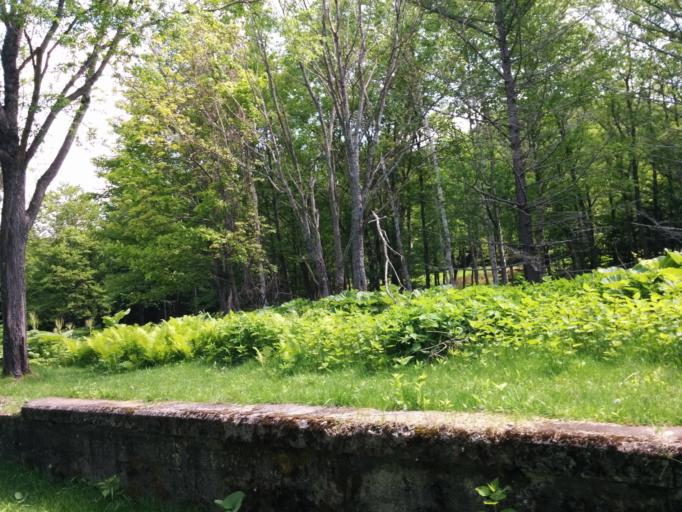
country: JP
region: Hokkaido
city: Otofuke
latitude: 43.4480
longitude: 143.1484
